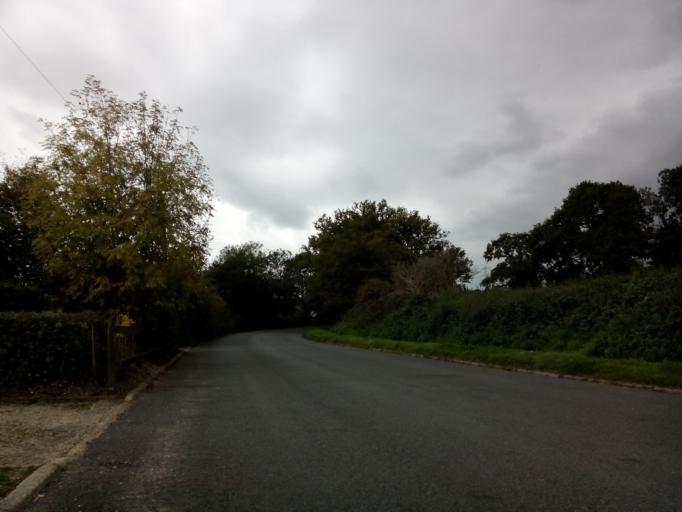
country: GB
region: England
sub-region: Suffolk
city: Ipswich
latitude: 52.0306
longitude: 1.1486
